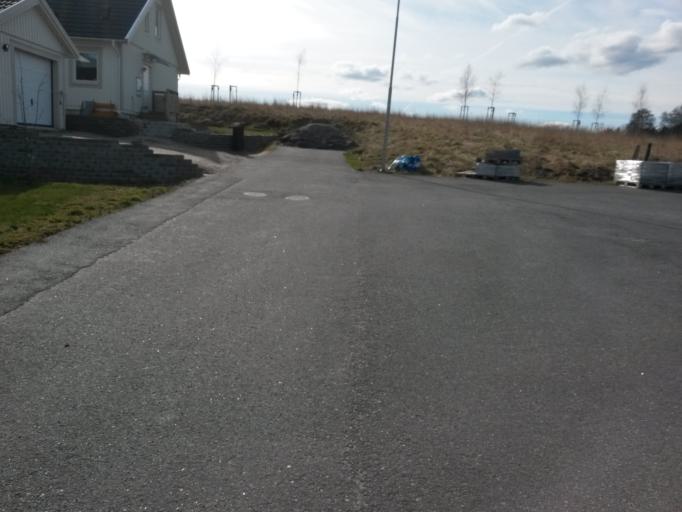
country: SE
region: Vaestra Goetaland
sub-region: Vargarda Kommun
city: Vargarda
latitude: 58.0243
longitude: 12.8050
